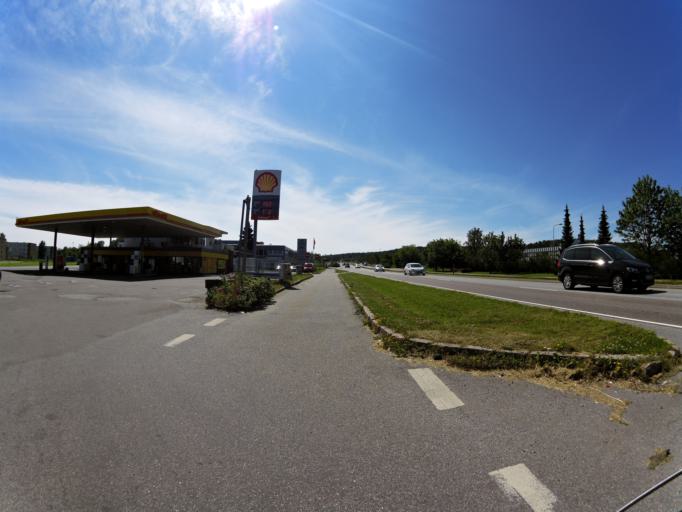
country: NO
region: Ostfold
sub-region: Fredrikstad
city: Fredrikstad
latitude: 59.2415
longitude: 10.9762
